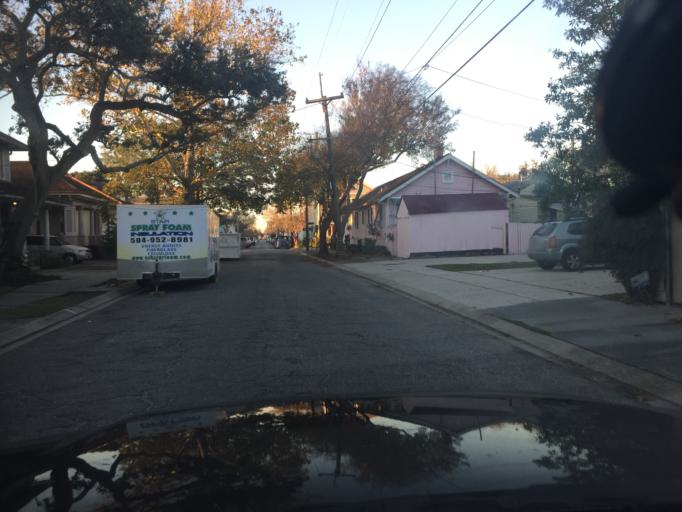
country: US
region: Louisiana
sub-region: Orleans Parish
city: New Orleans
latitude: 29.9766
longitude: -90.0849
